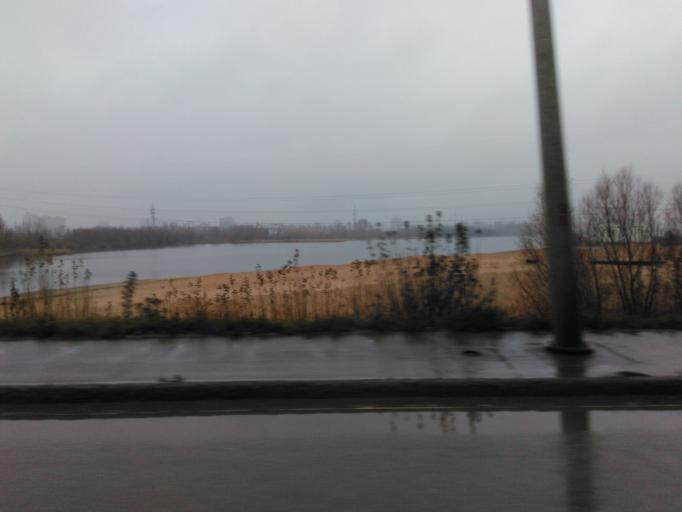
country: RU
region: Tatarstan
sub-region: Gorod Kazan'
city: Kazan
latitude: 55.7997
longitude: 49.0728
